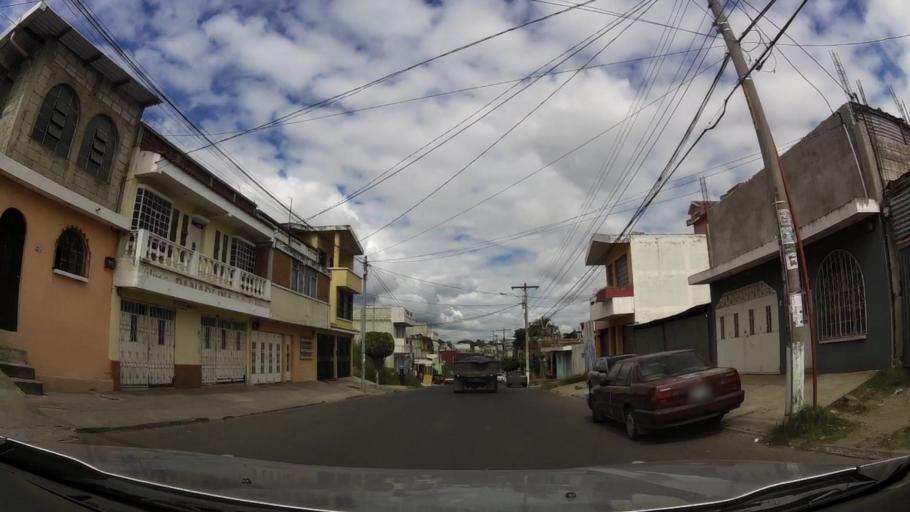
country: GT
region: Guatemala
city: Guatemala City
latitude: 14.6774
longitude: -90.5466
